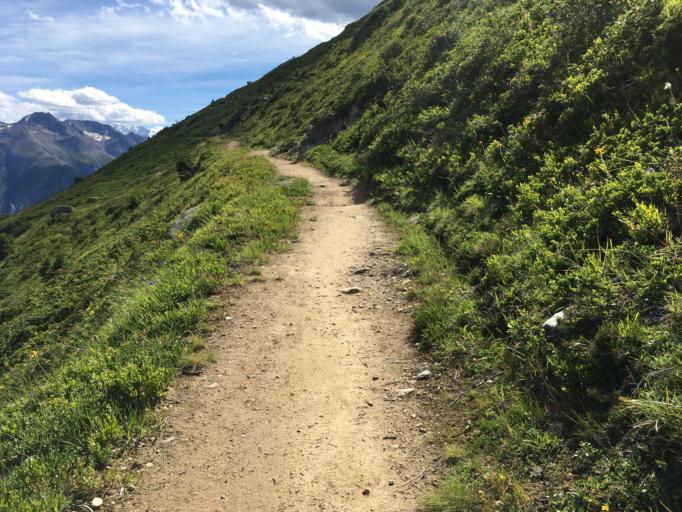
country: CH
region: Valais
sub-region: Goms District
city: Fiesch
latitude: 46.4312
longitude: 8.1193
